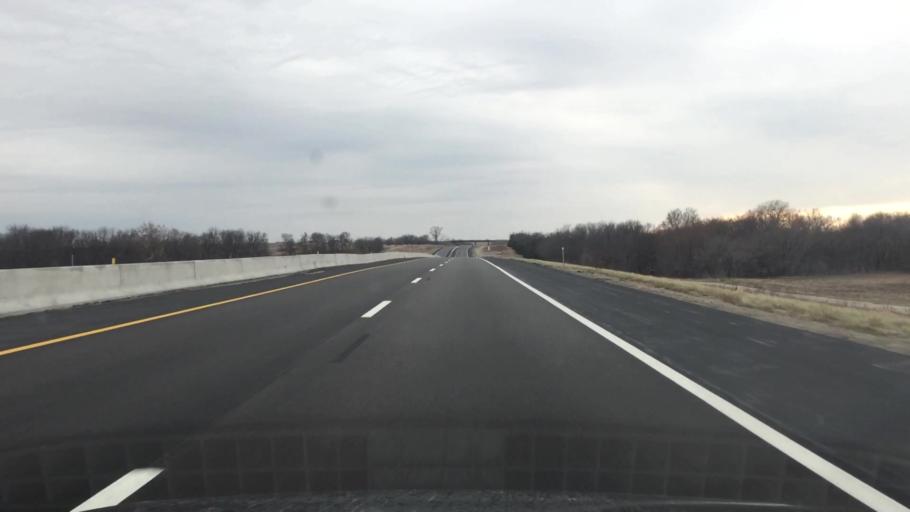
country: US
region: Kansas
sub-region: Shawnee County
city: Auburn
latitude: 38.7741
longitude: -95.9232
